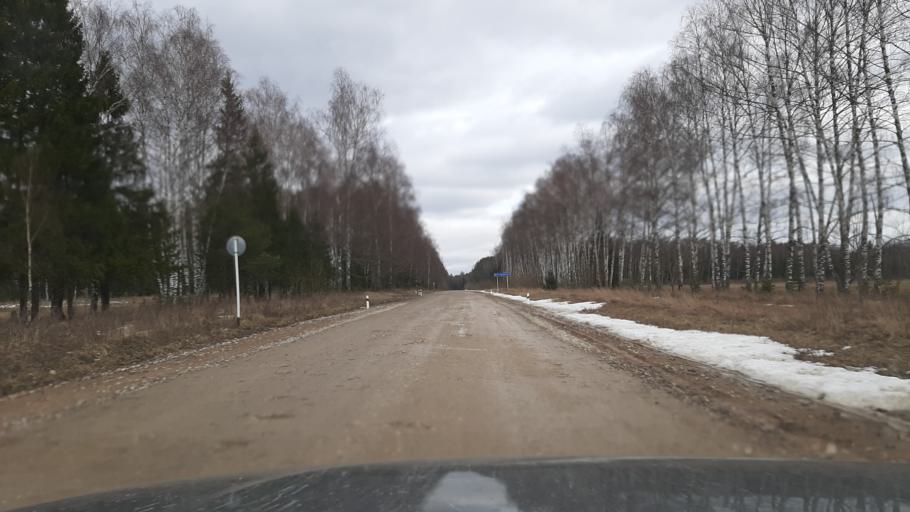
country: RU
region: Ivanovo
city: Teykovo
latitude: 56.8835
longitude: 40.6319
